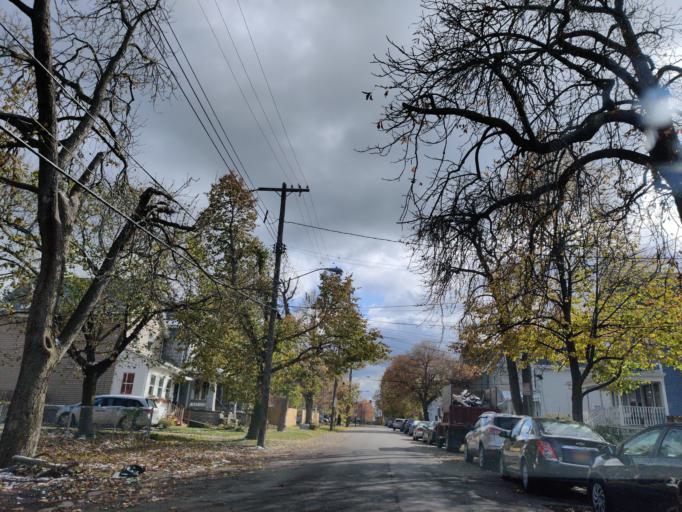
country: US
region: New York
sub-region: Erie County
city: Buffalo
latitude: 42.9049
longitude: -78.8871
